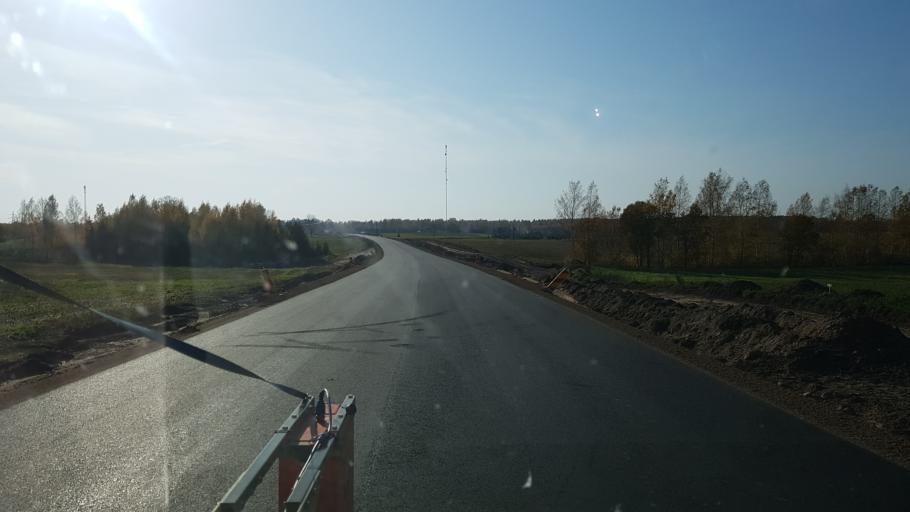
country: EE
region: Vorumaa
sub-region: Antsla vald
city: Vana-Antsla
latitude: 57.8420
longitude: 26.5531
